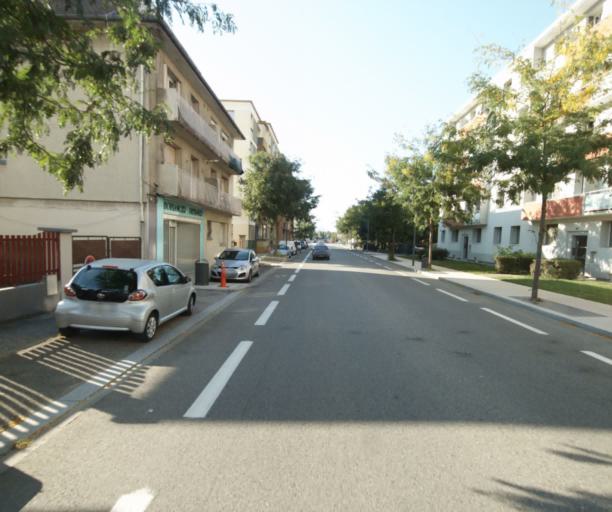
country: FR
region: Rhone-Alpes
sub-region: Departement de l'Isere
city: Fontaine
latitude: 45.1989
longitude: 5.6921
